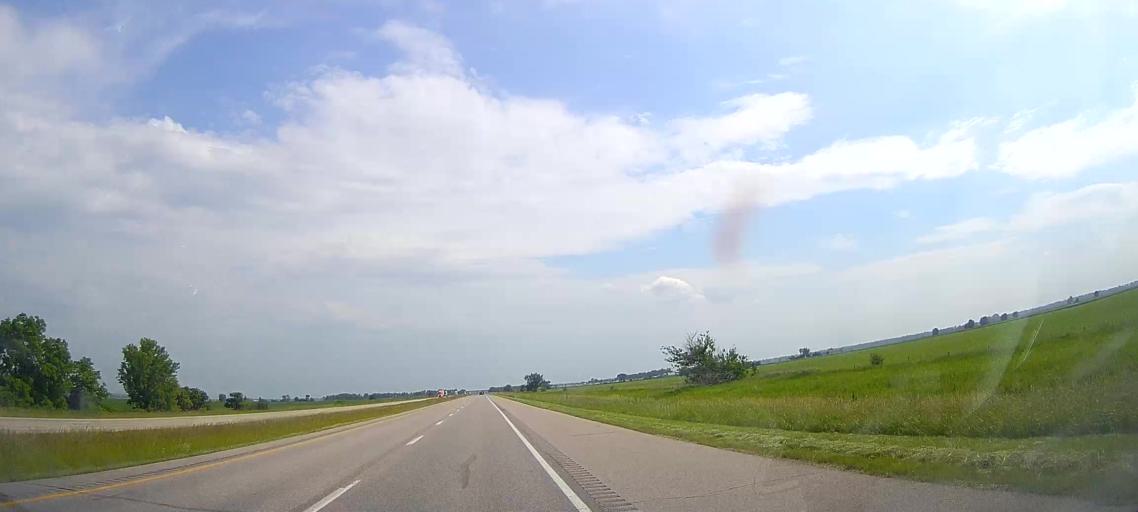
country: US
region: Iowa
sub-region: Monona County
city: Onawa
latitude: 41.9020
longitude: -96.1043
